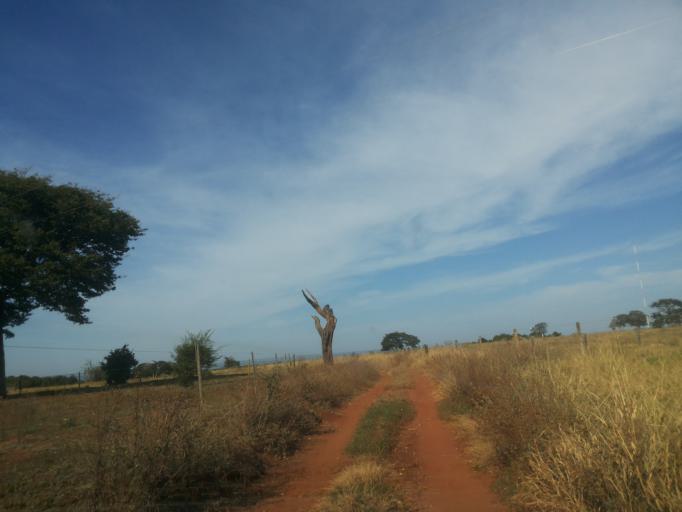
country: BR
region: Minas Gerais
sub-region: Ituiutaba
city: Ituiutaba
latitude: -19.1267
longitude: -49.3806
